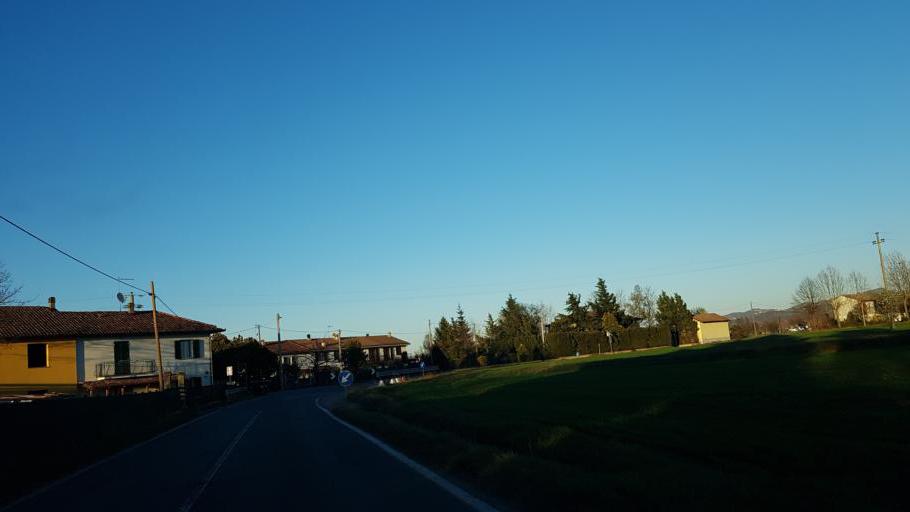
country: IT
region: Piedmont
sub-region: Provincia di Alessandria
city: Novi Ligure
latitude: 44.7813
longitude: 8.8156
